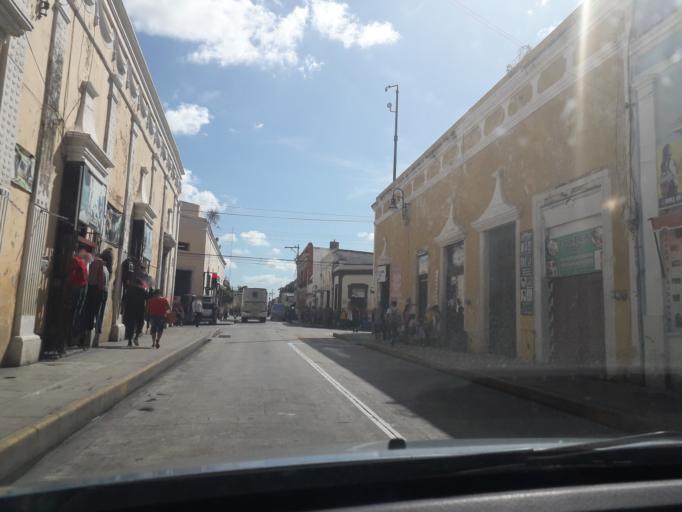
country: MX
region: Yucatan
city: Merida
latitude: 20.9639
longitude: -89.6250
